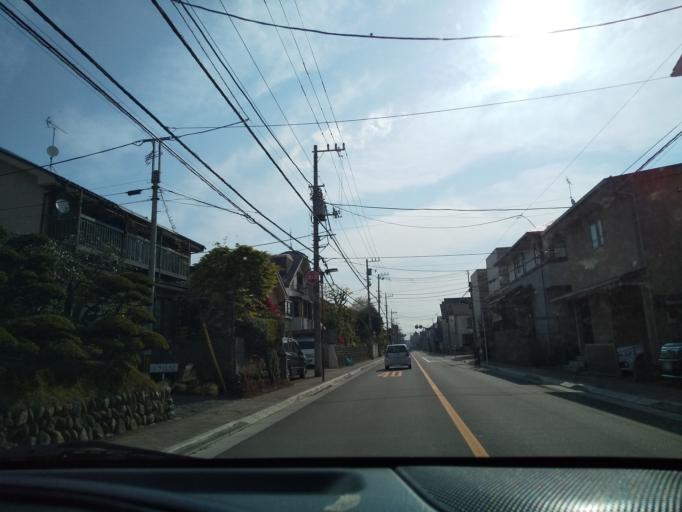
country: JP
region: Tokyo
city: Kokubunji
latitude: 35.6903
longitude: 139.4371
